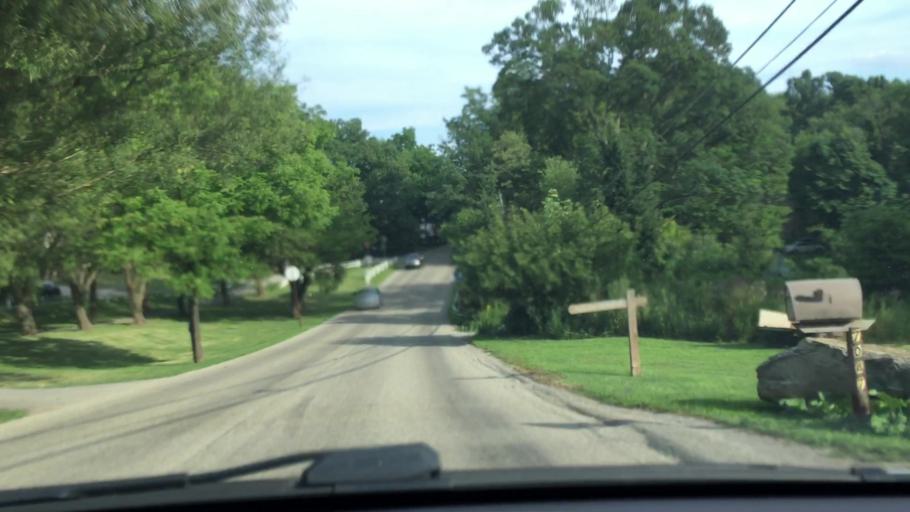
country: US
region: Pennsylvania
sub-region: Butler County
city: Seven Fields
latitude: 40.6792
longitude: -80.0711
